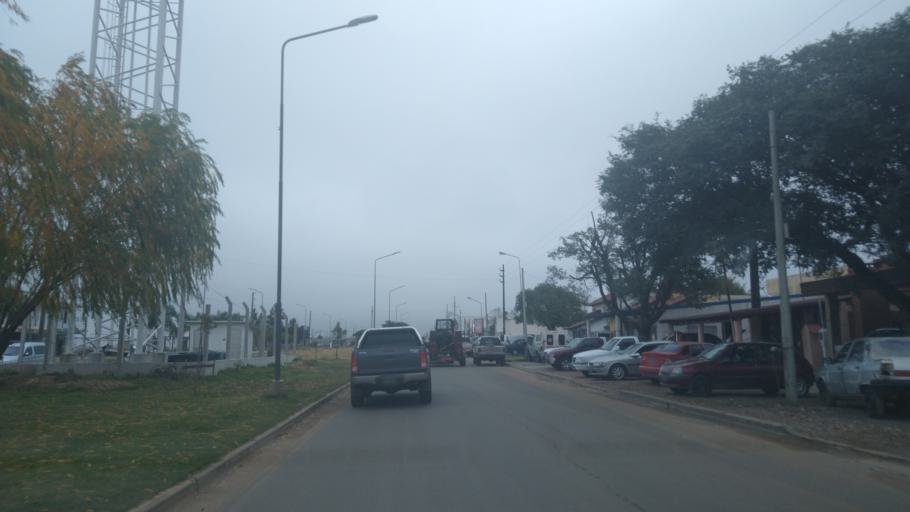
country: AR
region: Entre Rios
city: Chajari
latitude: -30.7608
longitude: -58.0024
